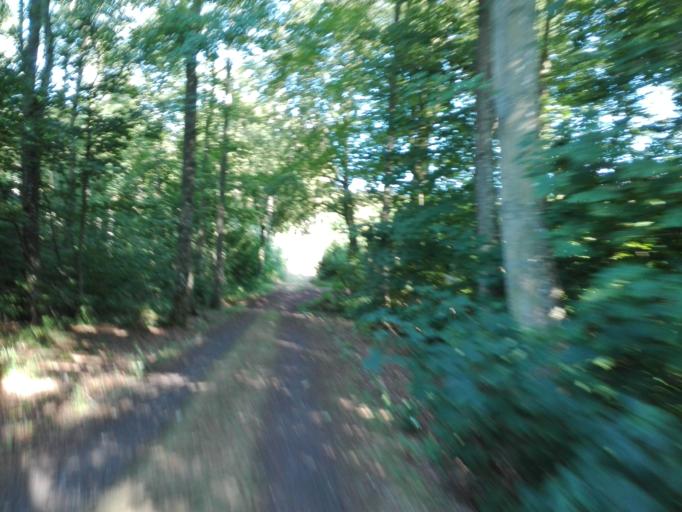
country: DK
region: Central Jutland
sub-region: Odder Kommune
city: Odder
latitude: 55.9527
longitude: 10.0831
